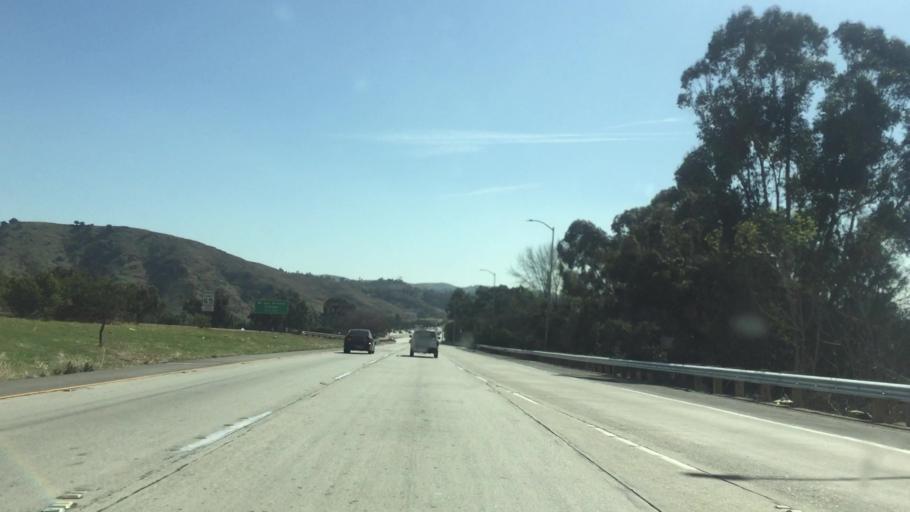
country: US
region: California
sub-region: Los Angeles County
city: Diamond Bar
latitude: 34.0612
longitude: -117.8059
